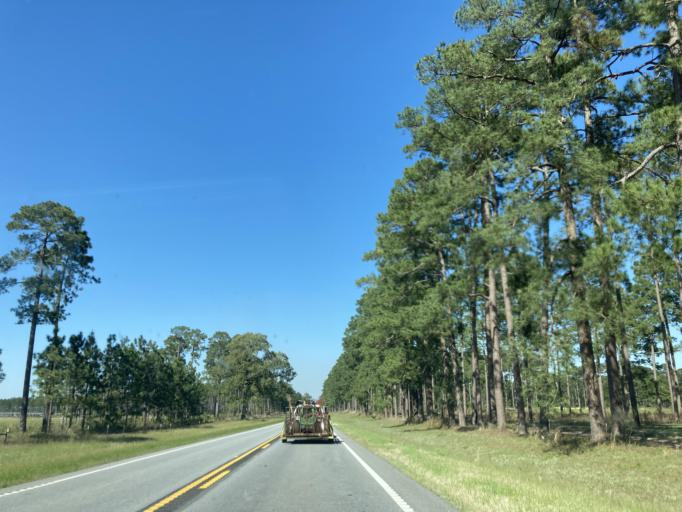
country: US
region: Georgia
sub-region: Baker County
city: Newton
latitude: 31.3527
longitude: -84.3007
